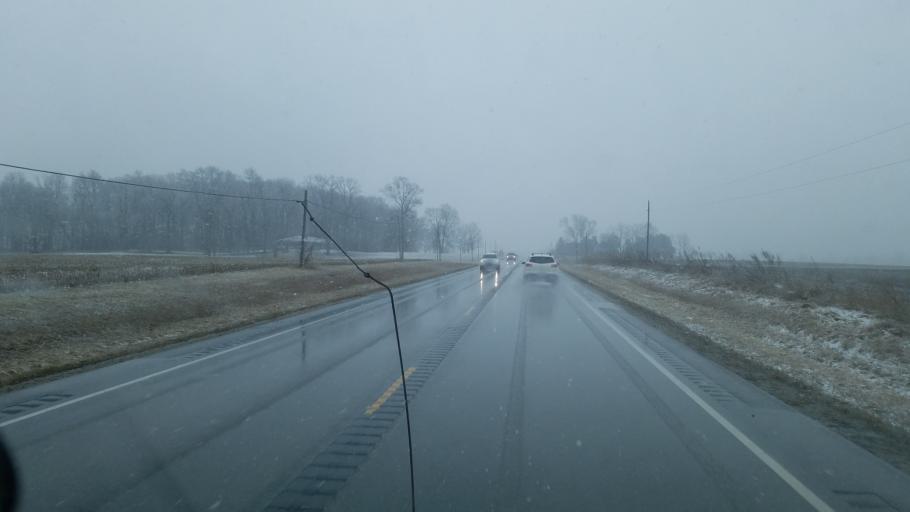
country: US
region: Indiana
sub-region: Grant County
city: Sweetser
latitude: 40.6362
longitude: -85.7081
